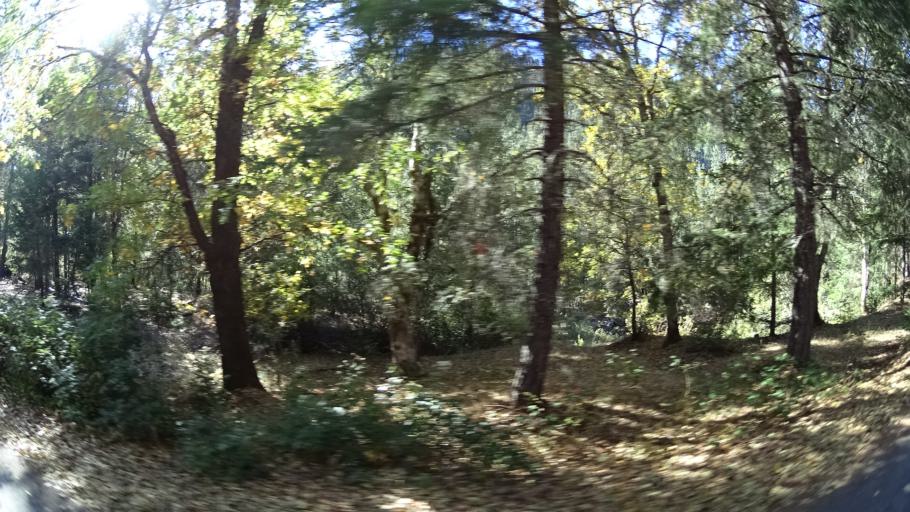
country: US
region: California
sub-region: Trinity County
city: Weaverville
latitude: 41.1410
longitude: -123.1427
